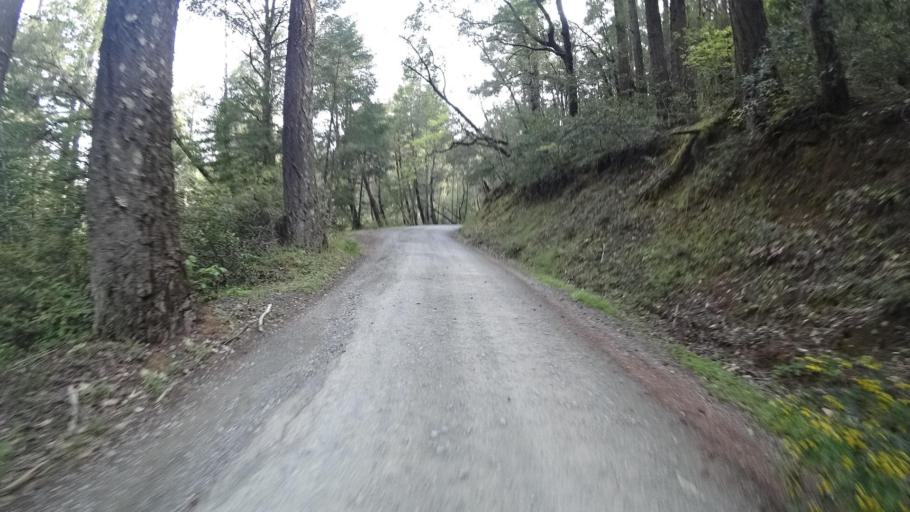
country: US
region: California
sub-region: Humboldt County
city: Redway
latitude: 40.2391
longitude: -123.8139
